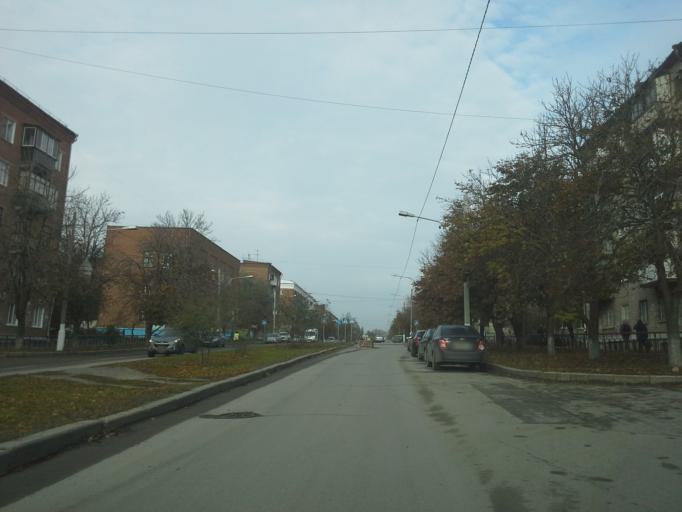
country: RU
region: Volgograd
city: Vodstroy
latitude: 48.7813
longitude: 44.5689
